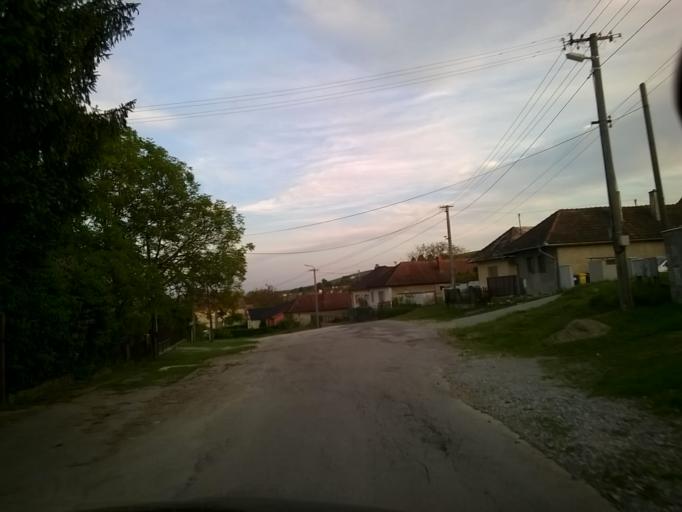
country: SK
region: Nitriansky
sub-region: Okres Nitra
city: Nitra
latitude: 48.3779
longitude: 18.1749
